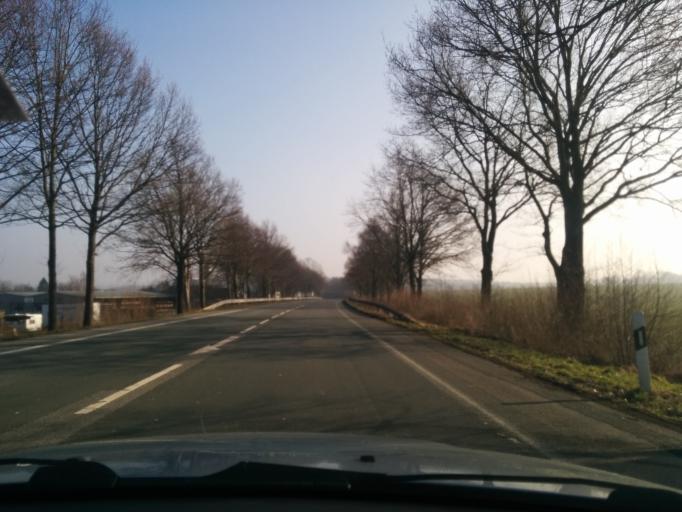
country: DE
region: North Rhine-Westphalia
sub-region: Regierungsbezirk Detmold
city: Lemgo
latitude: 52.0106
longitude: 8.9416
